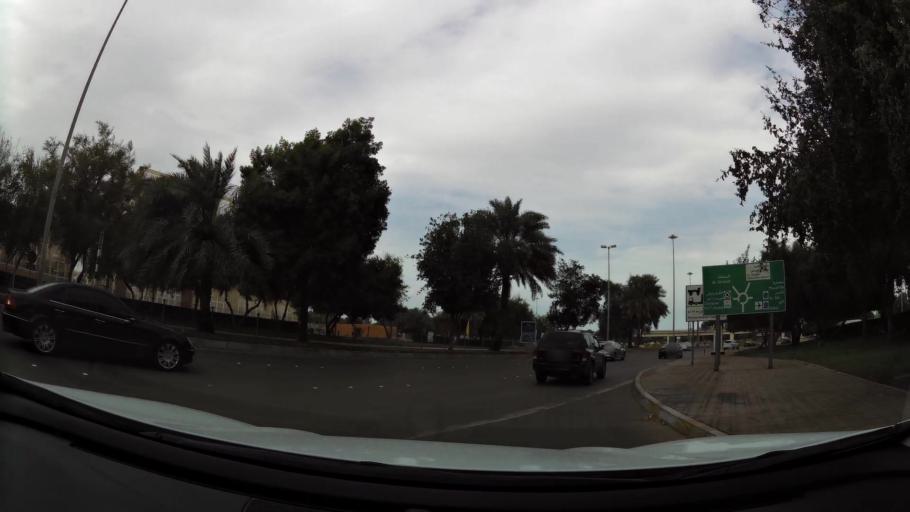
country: AE
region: Abu Dhabi
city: Abu Dhabi
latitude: 24.4242
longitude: 54.4449
